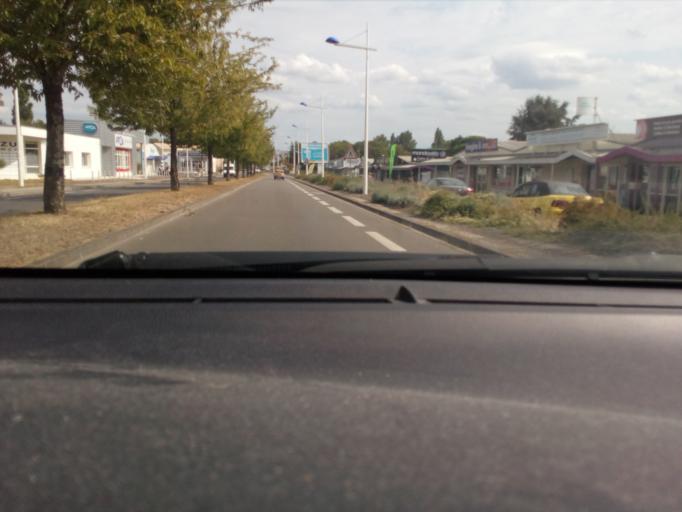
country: FR
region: Poitou-Charentes
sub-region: Departement de la Charente
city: Angouleme
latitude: 45.6634
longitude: 0.1539
